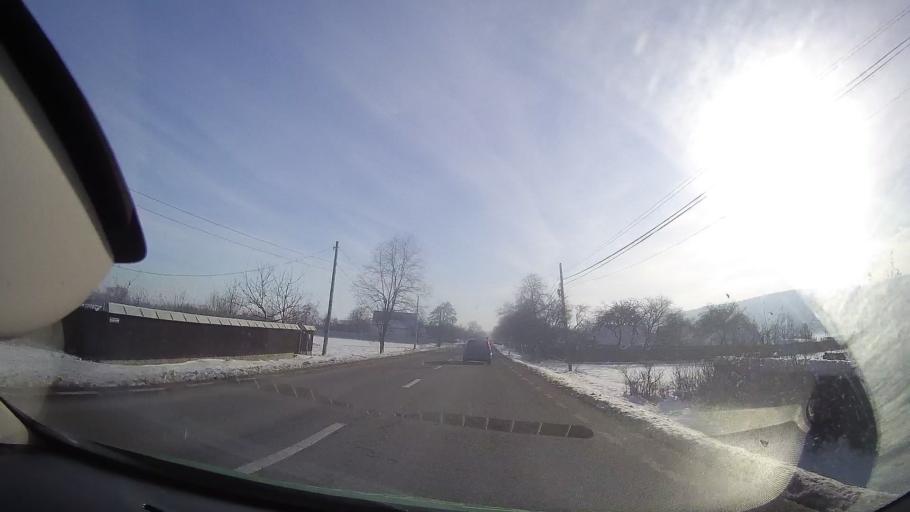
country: RO
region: Neamt
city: Bodesti
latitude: 47.0456
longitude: 26.4049
